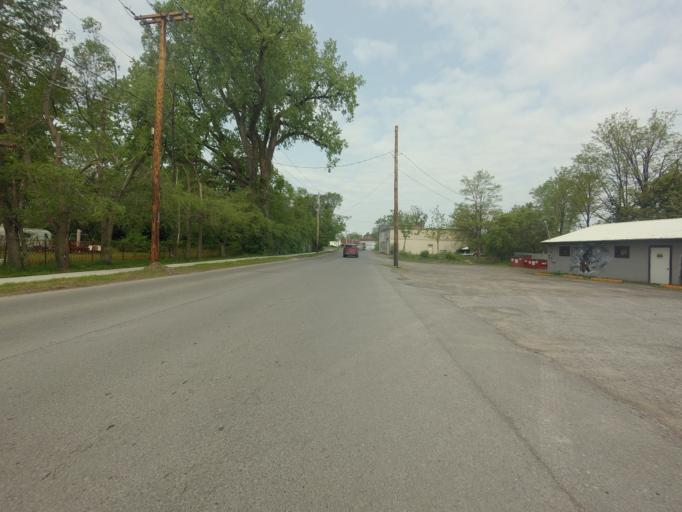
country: US
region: New York
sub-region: Jefferson County
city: Watertown
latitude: 43.9768
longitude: -75.8963
